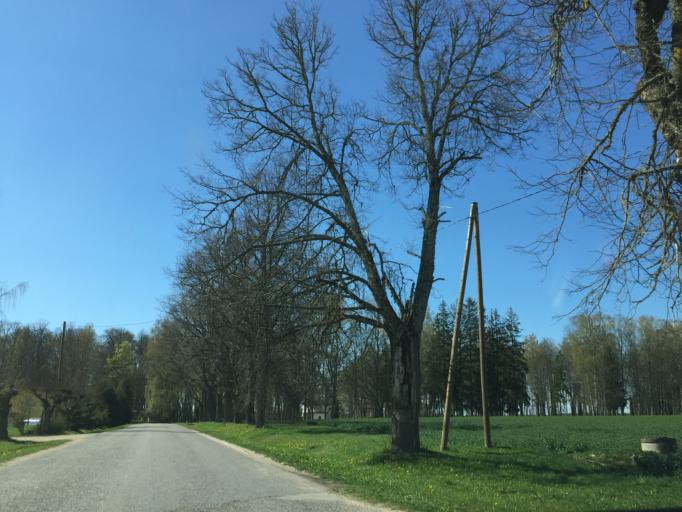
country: LV
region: Strenci
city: Strenci
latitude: 57.5427
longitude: 25.7072
